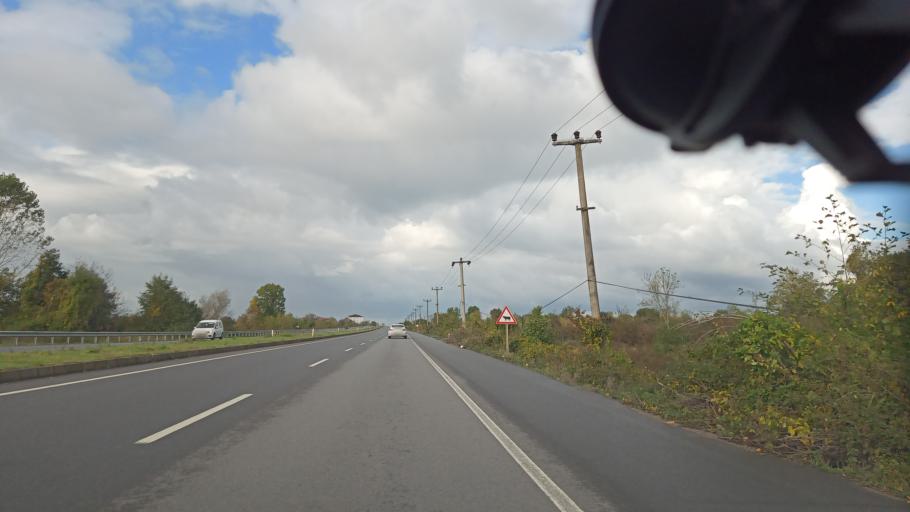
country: TR
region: Sakarya
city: Karasu
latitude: 41.0706
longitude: 30.7954
